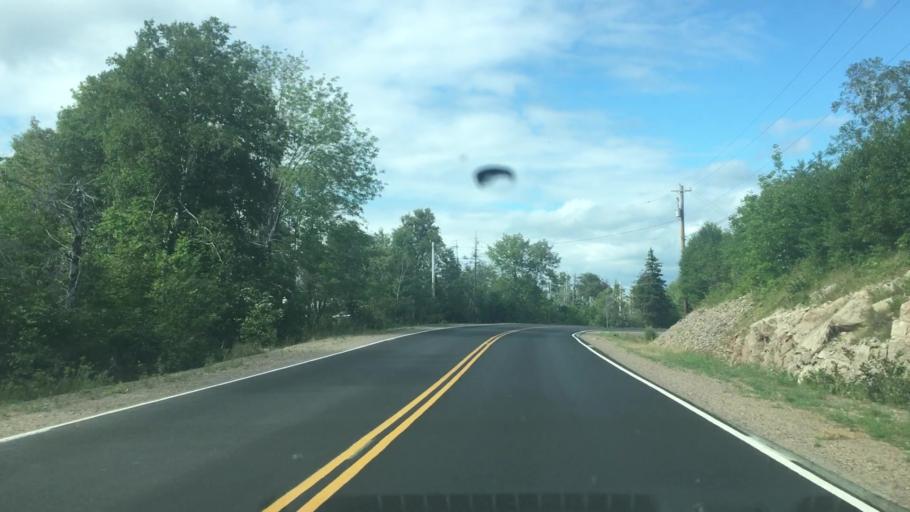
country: CA
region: Nova Scotia
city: Princeville
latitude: 45.7937
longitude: -60.7370
